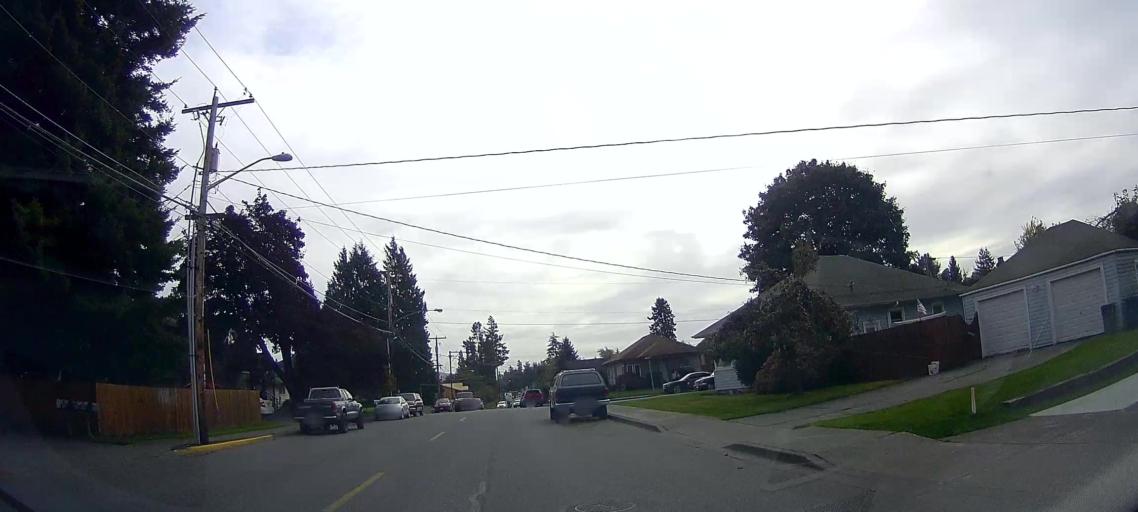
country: US
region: Washington
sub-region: Skagit County
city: Burlington
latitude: 48.4728
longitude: -122.3193
